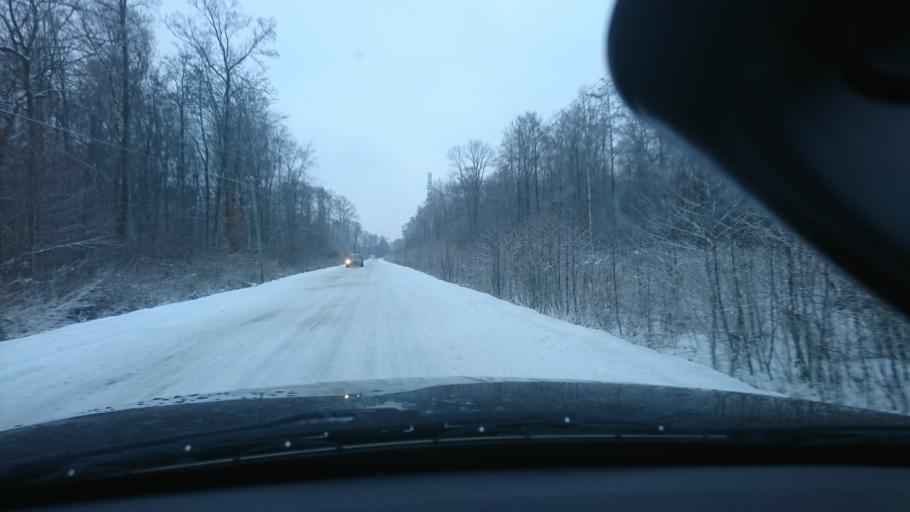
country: PL
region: Masovian Voivodeship
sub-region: Powiat ciechanowski
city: Glinojeck
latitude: 52.7491
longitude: 20.3100
